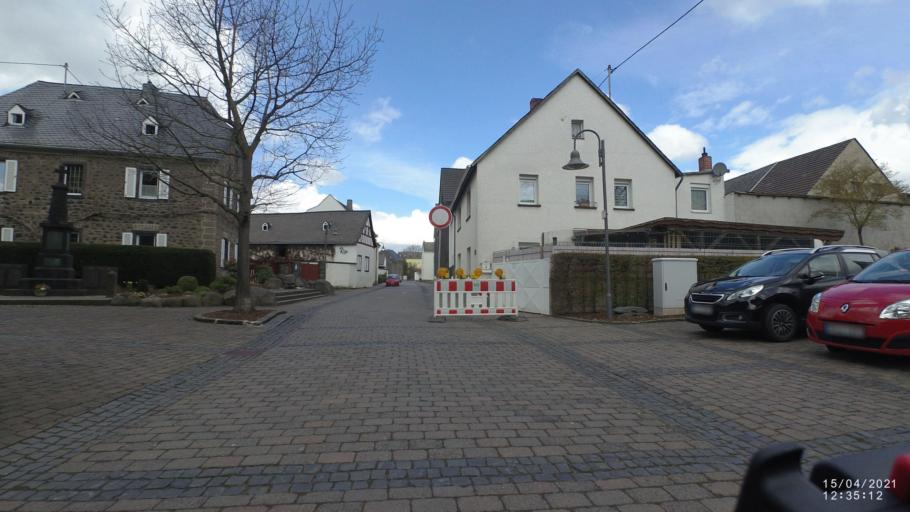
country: DE
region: Rheinland-Pfalz
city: Thur
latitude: 50.3577
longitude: 7.2755
